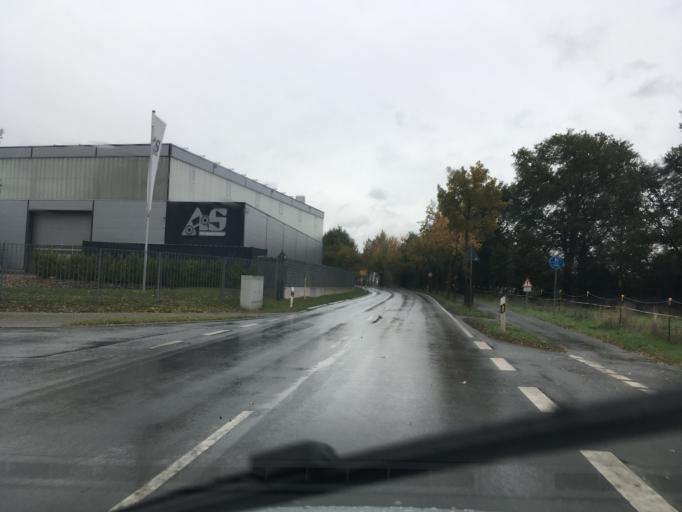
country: DE
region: North Rhine-Westphalia
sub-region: Regierungsbezirk Munster
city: Klein Reken
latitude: 51.8076
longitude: 7.0528
